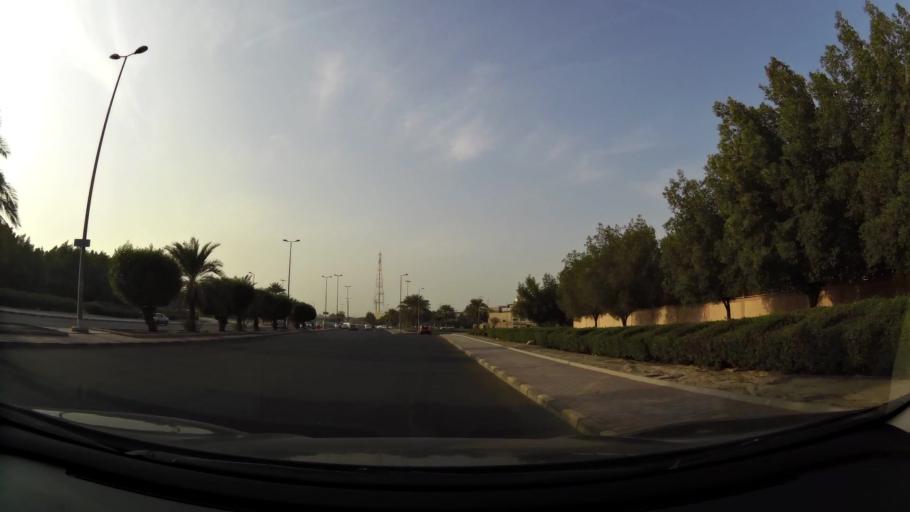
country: KW
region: Mubarak al Kabir
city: Sabah as Salim
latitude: 29.2483
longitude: 48.0684
